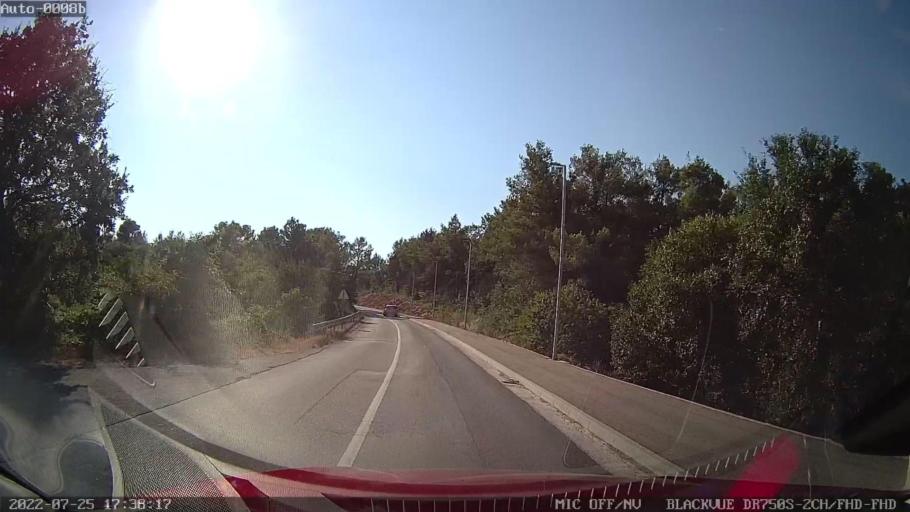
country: HR
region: Zadarska
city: Posedarje
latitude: 44.2090
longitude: 15.4636
